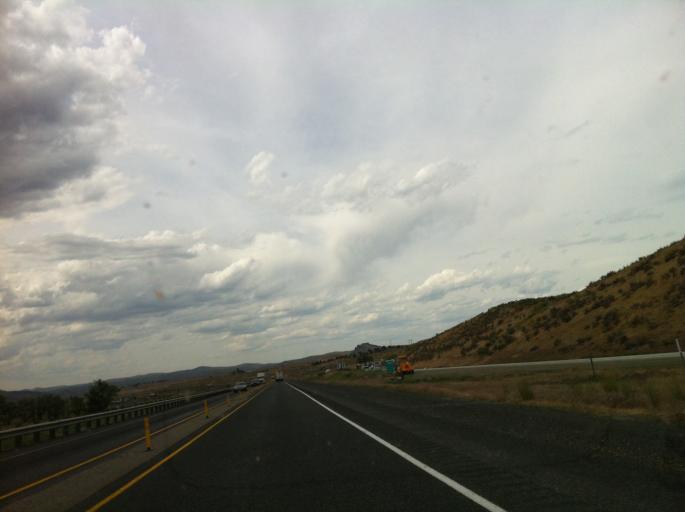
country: US
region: Oregon
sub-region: Baker County
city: Baker City
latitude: 44.5501
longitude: -117.4225
